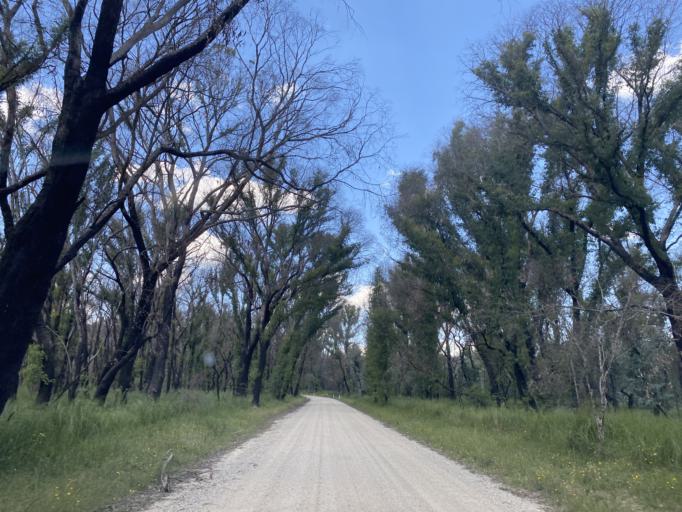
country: AU
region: Victoria
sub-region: Cardinia
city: Garfield
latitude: -37.9889
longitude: 145.6909
